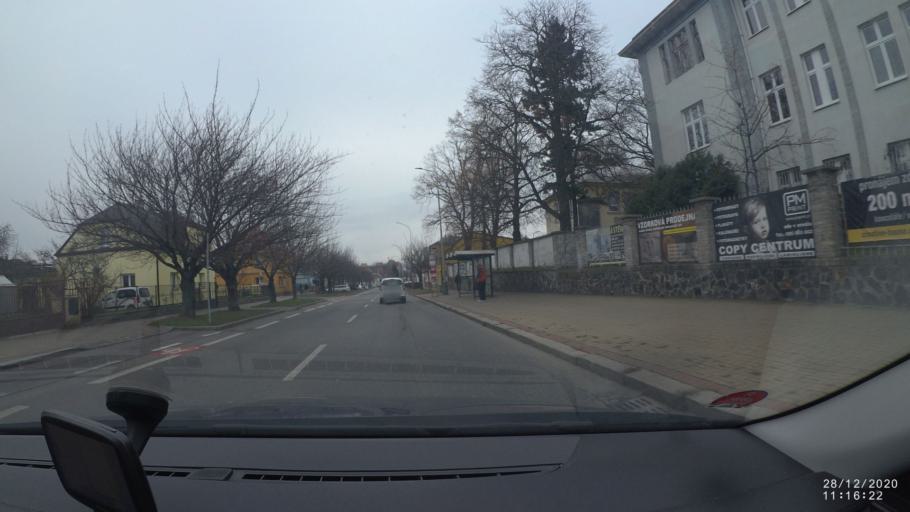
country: CZ
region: Praha
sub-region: Praha 18
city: Letnany
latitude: 50.1353
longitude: 14.5141
